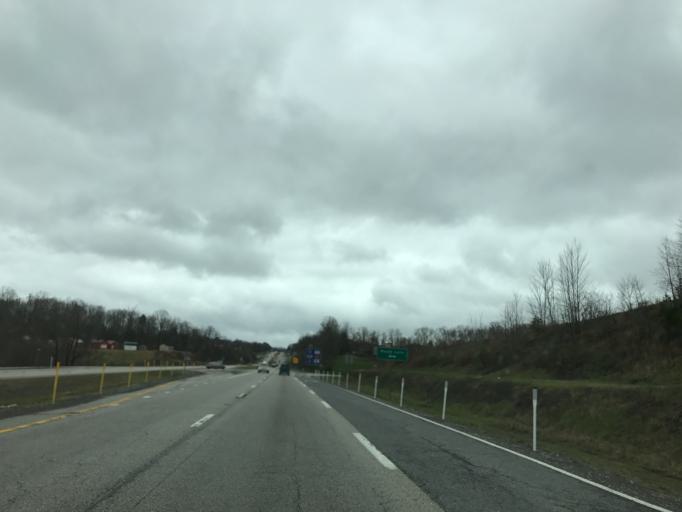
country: US
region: West Virginia
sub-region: Fayette County
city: Fayetteville
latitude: 38.0409
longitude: -81.1228
